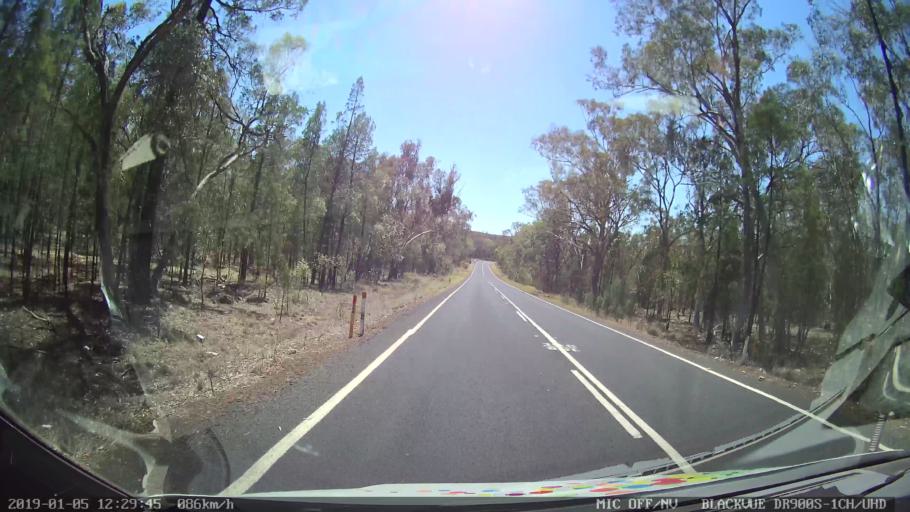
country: AU
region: New South Wales
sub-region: Warrumbungle Shire
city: Coonabarabran
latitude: -31.2315
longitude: 149.3406
